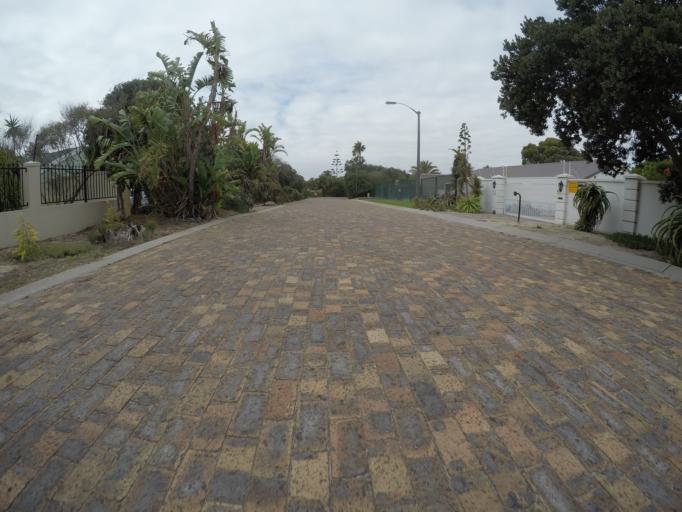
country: ZA
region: Western Cape
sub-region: City of Cape Town
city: Atlantis
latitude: -33.6924
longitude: 18.4415
